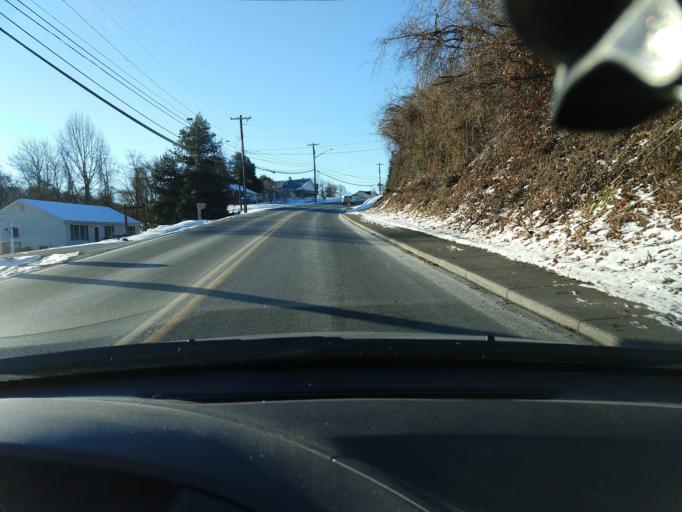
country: US
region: Virginia
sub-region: City of Bedford
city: Bedford
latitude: 37.3298
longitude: -79.5282
